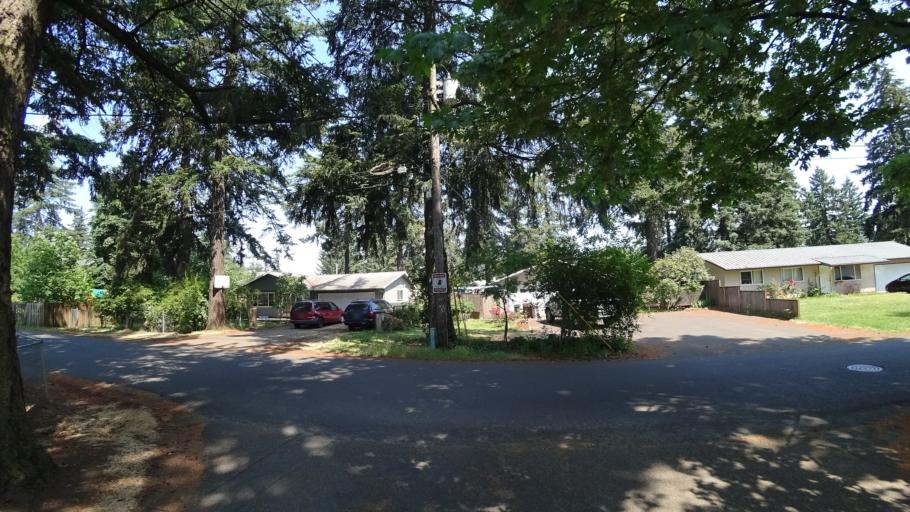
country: US
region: Oregon
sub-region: Multnomah County
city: Lents
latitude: 45.4510
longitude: -122.5896
